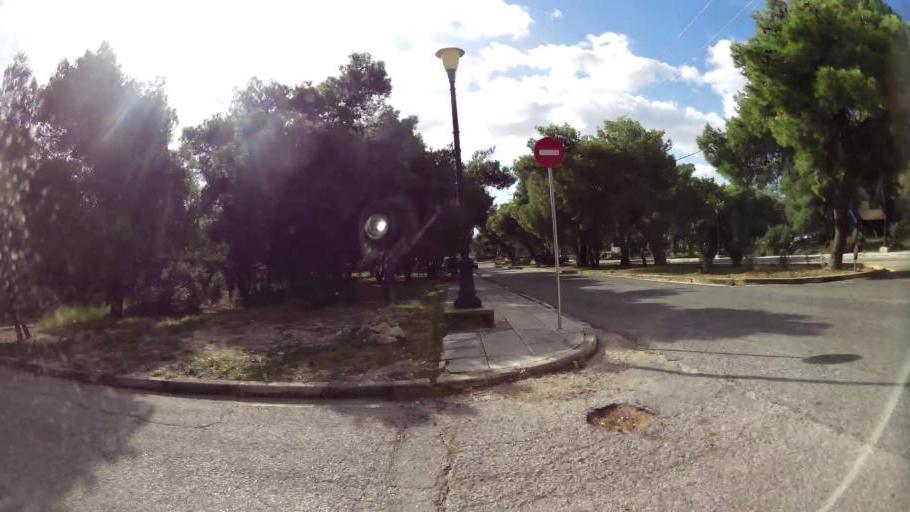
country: GR
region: Attica
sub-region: Nomarchia Anatolikis Attikis
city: Thrakomakedones
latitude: 38.1314
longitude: 23.7573
